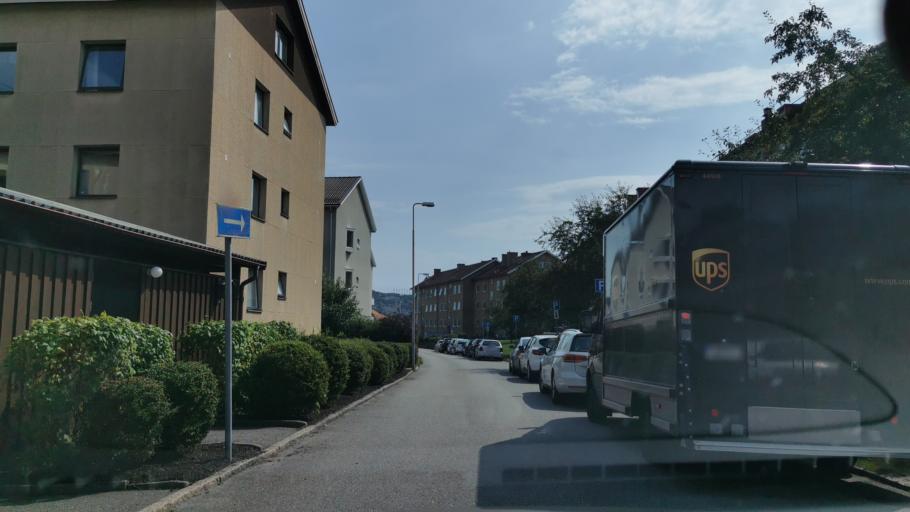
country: SE
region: Vaestra Goetaland
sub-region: Molndal
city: Moelndal
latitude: 57.6754
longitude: 11.9924
